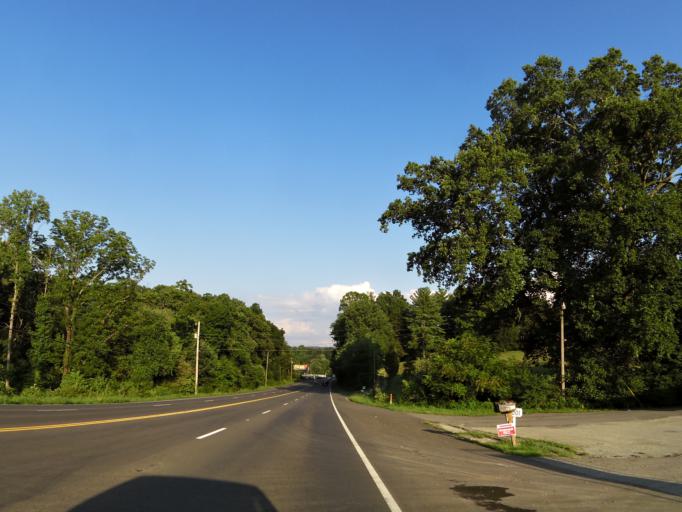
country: US
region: Tennessee
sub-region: Anderson County
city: Clinton
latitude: 36.0290
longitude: -84.0668
